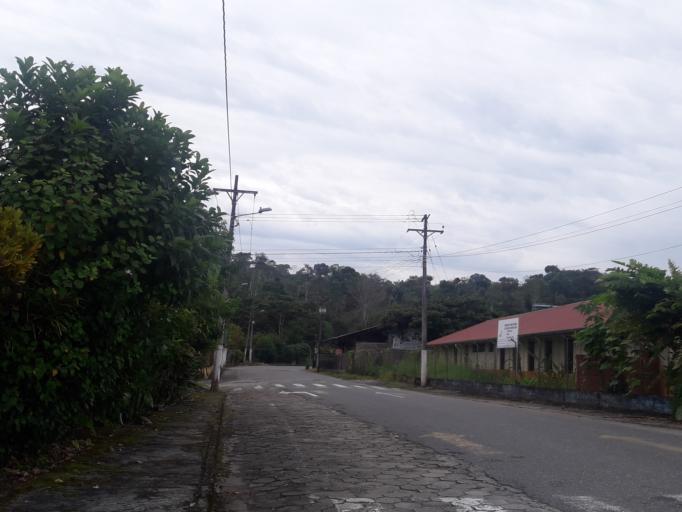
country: EC
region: Napo
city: Tena
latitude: -1.0425
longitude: -77.7917
